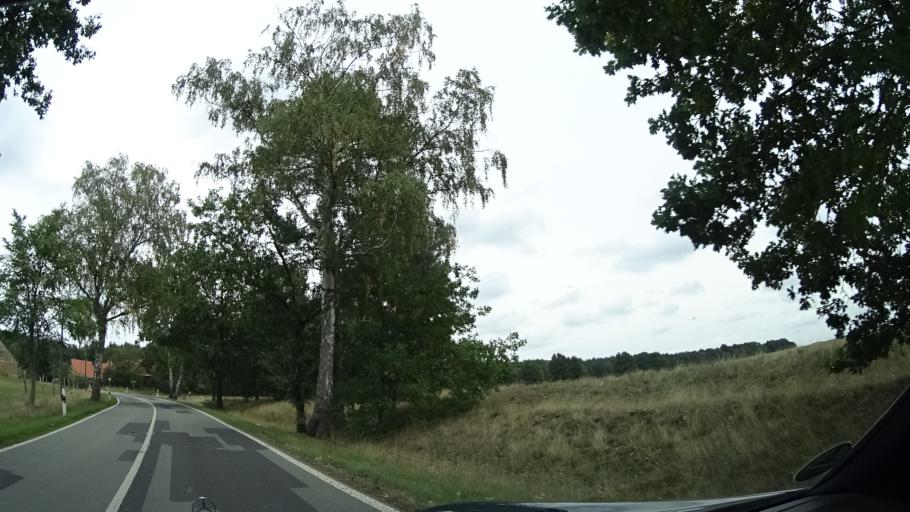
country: DE
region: Brandenburg
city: Walsleben
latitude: 52.9655
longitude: 12.7181
